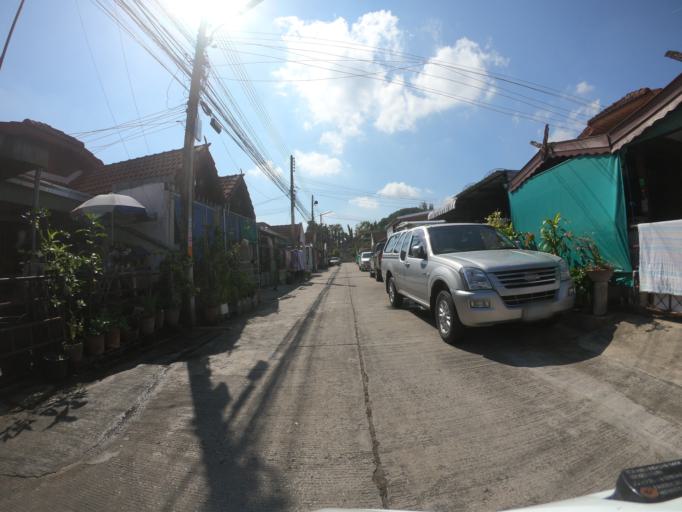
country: TH
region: Chiang Mai
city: Chiang Mai
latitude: 18.7427
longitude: 98.9524
